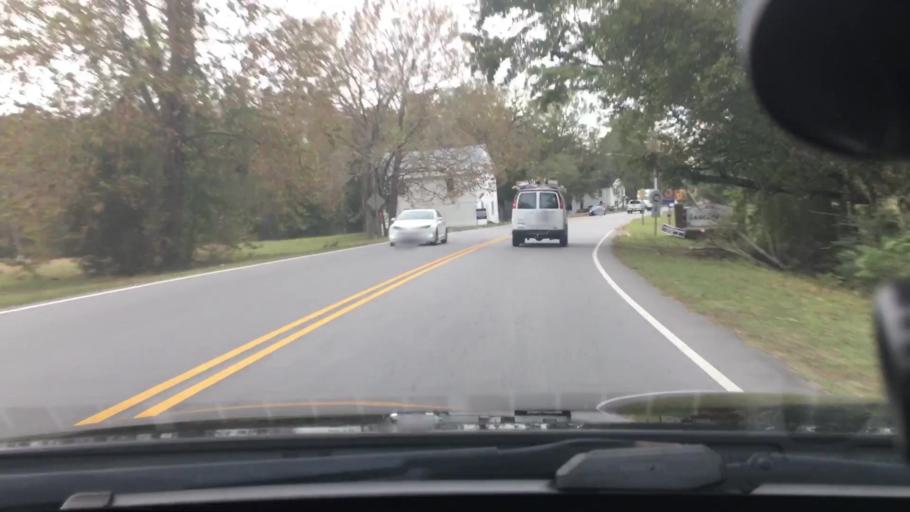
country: US
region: North Carolina
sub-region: Craven County
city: Vanceboro
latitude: 35.2953
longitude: -77.1464
